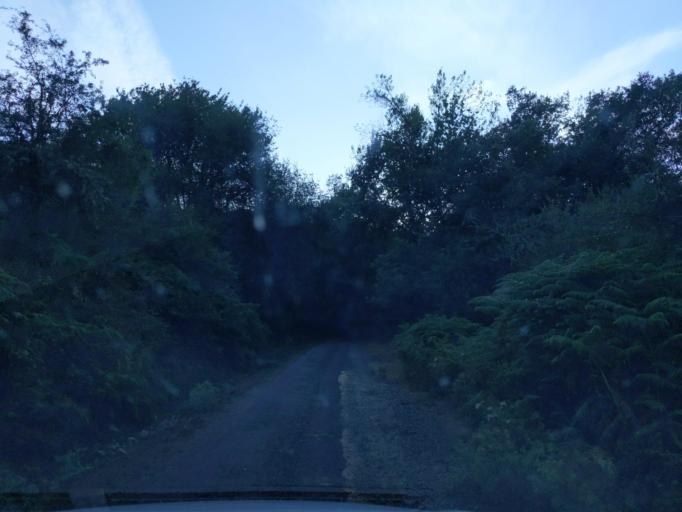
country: ES
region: La Rioja
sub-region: Provincia de La Rioja
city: Ojacastro
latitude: 42.3787
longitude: -3.0152
